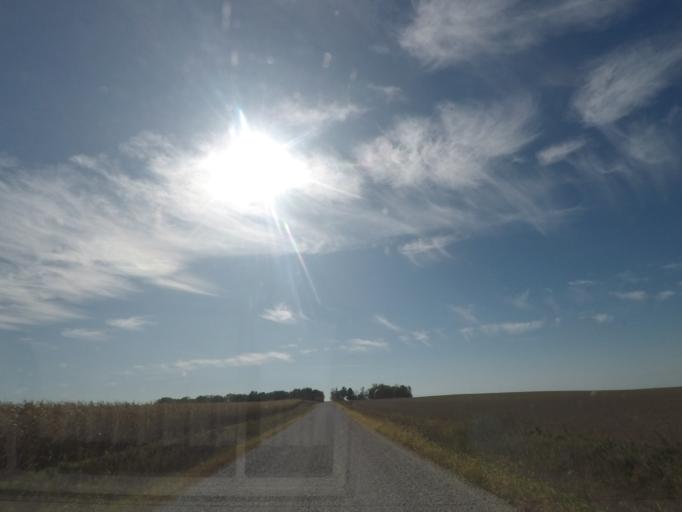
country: US
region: Iowa
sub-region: Story County
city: Nevada
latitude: 42.0540
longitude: -93.3290
